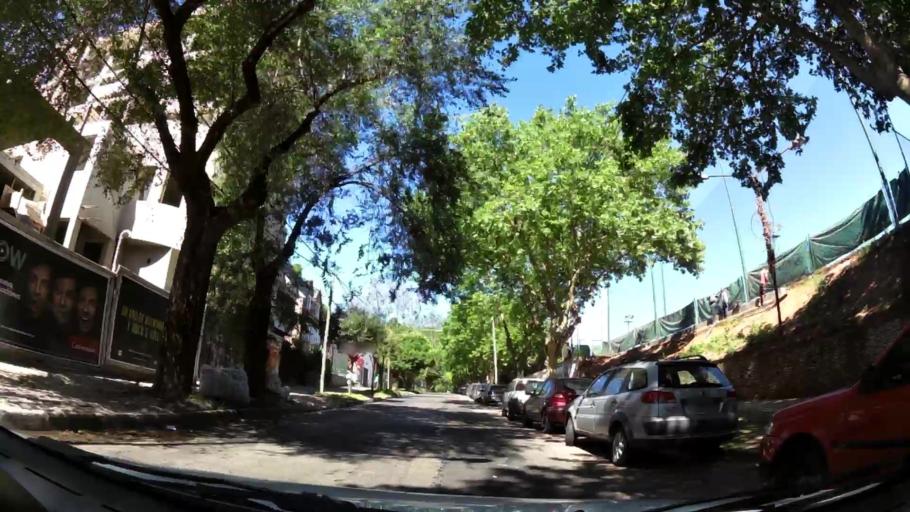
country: AR
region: Buenos Aires
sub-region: Partido de Vicente Lopez
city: Olivos
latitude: -34.5177
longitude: -58.4787
